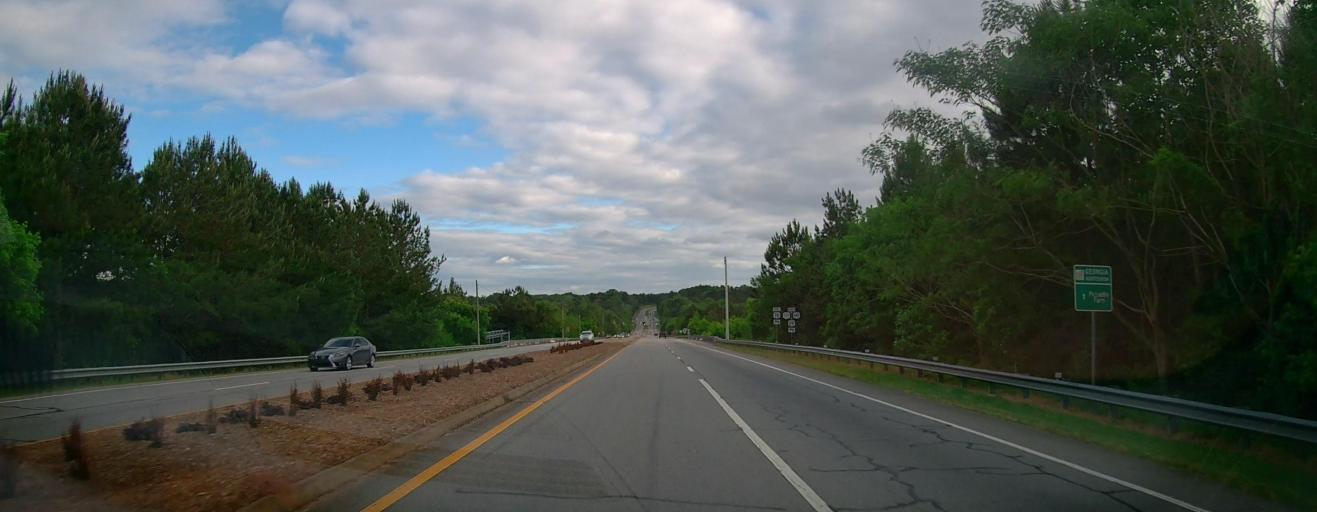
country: US
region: Georgia
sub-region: Clarke County
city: Athens
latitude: 33.9179
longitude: -83.4054
